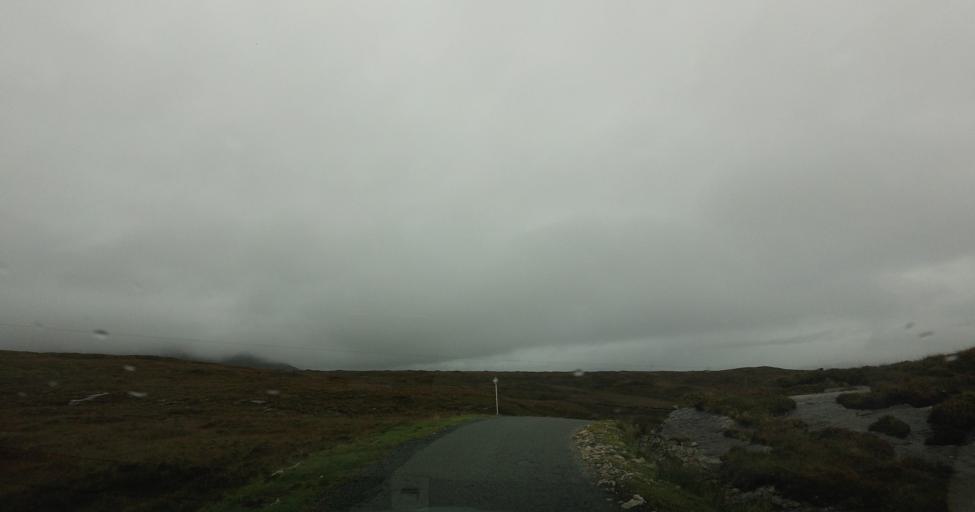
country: GB
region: Scotland
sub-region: Highland
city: Isle of Skye
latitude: 57.1436
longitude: -6.0792
